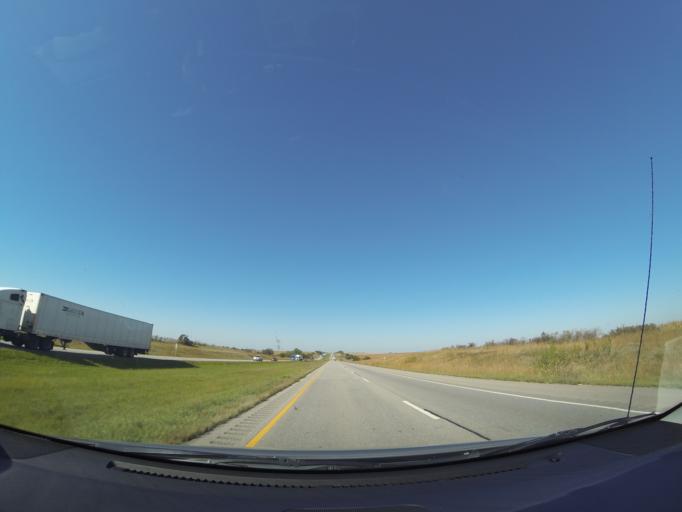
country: US
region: Nebraska
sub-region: Seward County
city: Seward
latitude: 40.8224
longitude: -97.1300
